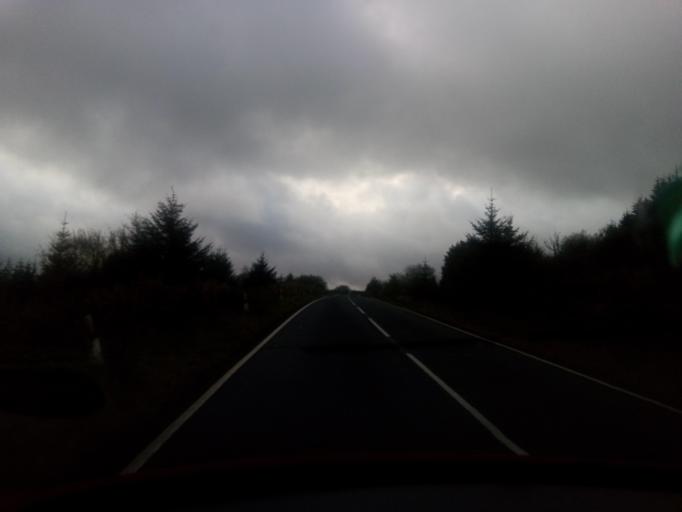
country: GB
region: Scotland
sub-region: The Scottish Borders
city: Hawick
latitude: 55.3270
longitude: -2.6469
